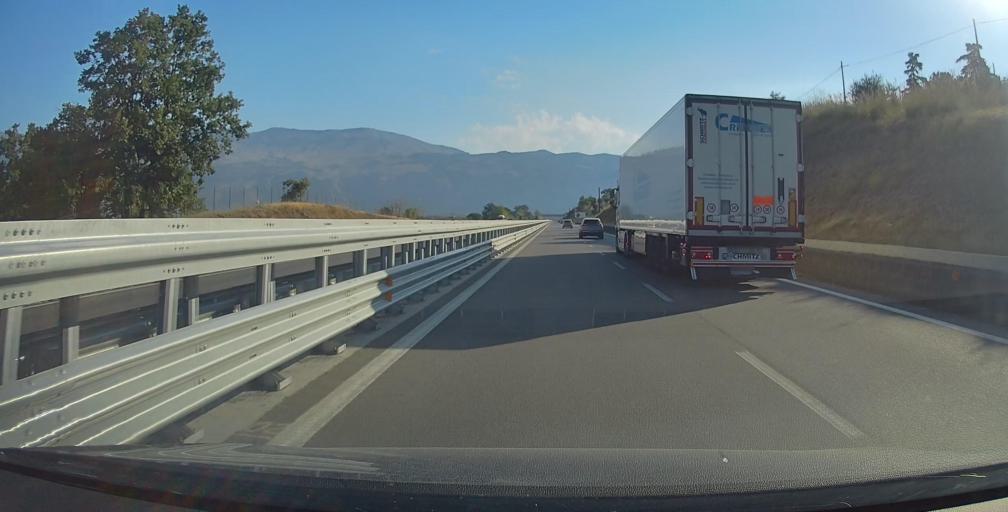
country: IT
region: Calabria
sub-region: Provincia di Cosenza
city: Castrovillari
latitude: 39.8031
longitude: 16.2424
